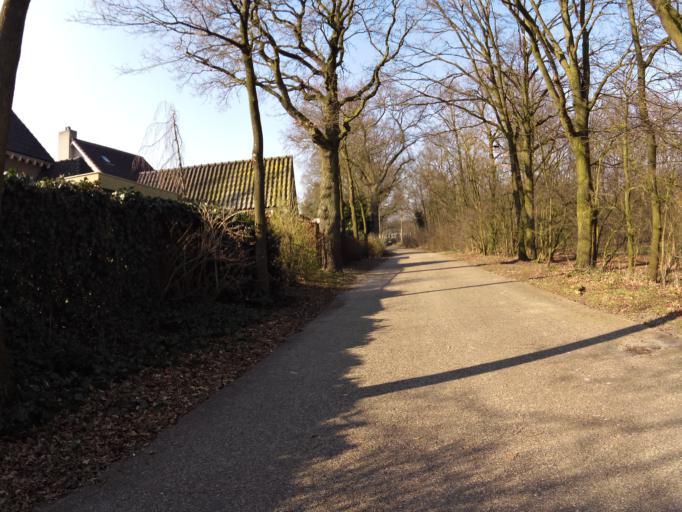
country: NL
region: North Brabant
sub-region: Gemeente Sint-Michielsgestel
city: Sint-Michielsgestel
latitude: 51.7125
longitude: 5.3835
